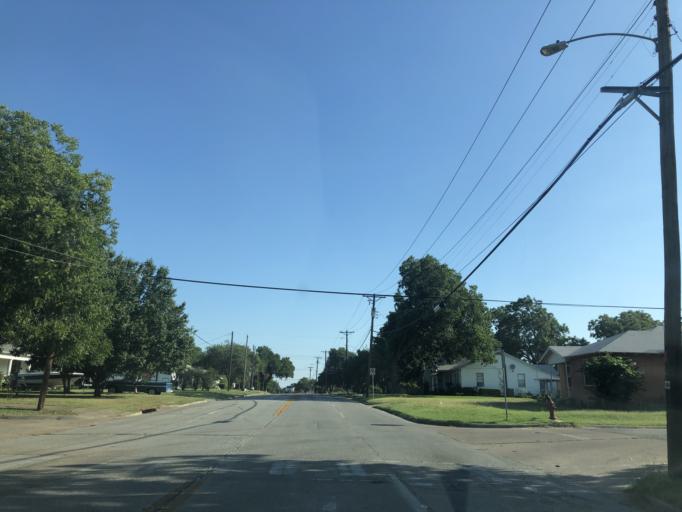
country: US
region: Texas
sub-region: Dallas County
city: Grand Prairie
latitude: 32.7406
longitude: -97.0056
